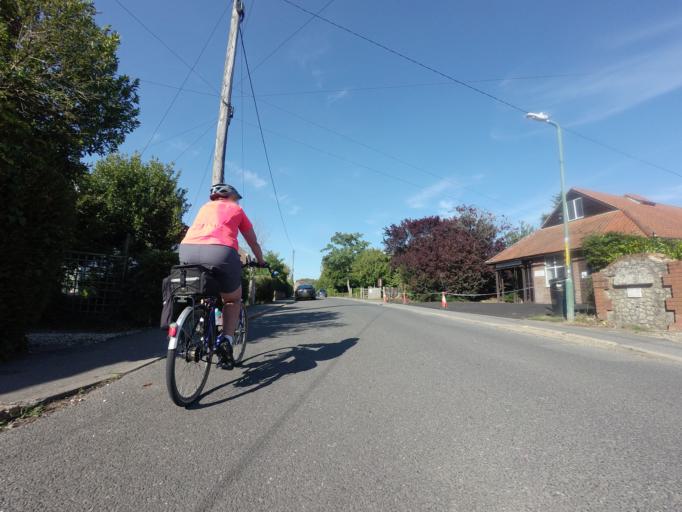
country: GB
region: England
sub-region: Kent
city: Tenterden
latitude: 51.0124
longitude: 0.7065
